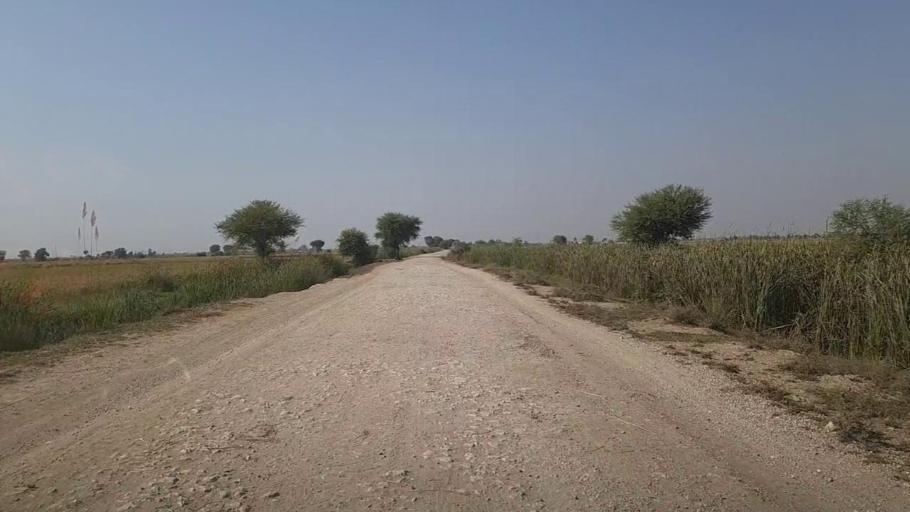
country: PK
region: Sindh
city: Kandhkot
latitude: 28.3996
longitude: 69.2658
